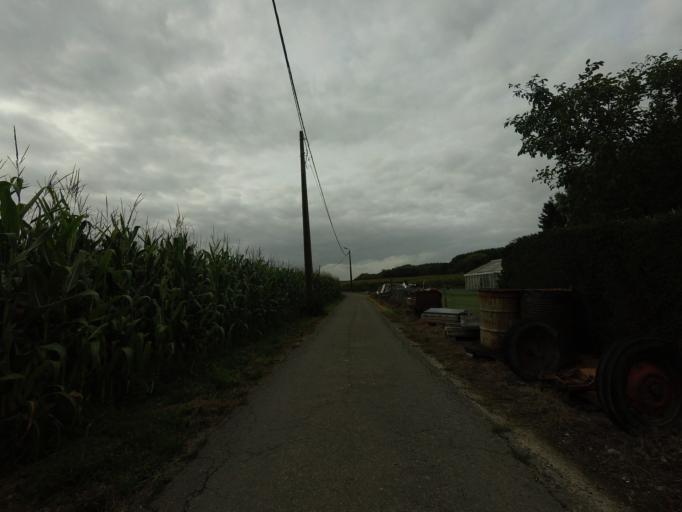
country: BE
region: Flanders
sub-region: Provincie Vlaams-Brabant
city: Meise
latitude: 50.9712
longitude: 4.3265
